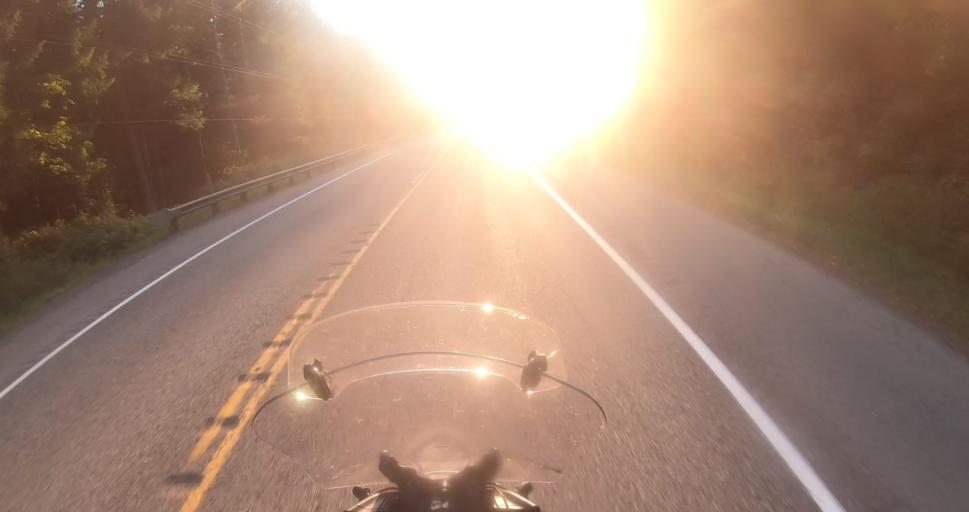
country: US
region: Washington
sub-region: Lewis County
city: Morton
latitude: 46.5363
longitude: -122.0015
